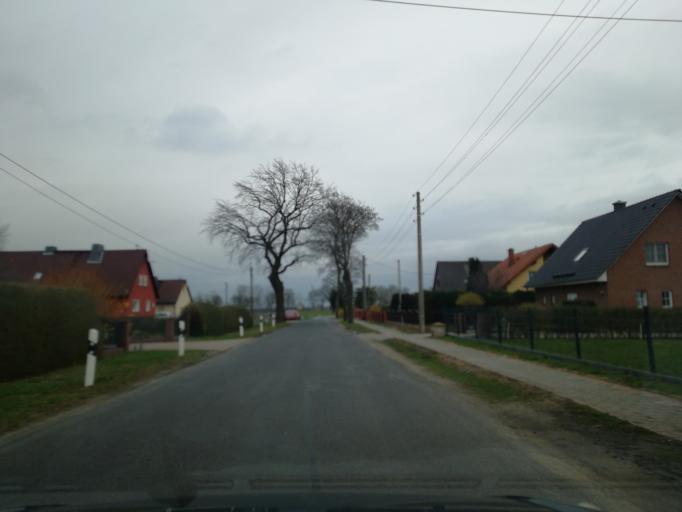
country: DE
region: Brandenburg
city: Calau
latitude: 51.7298
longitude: 14.0225
